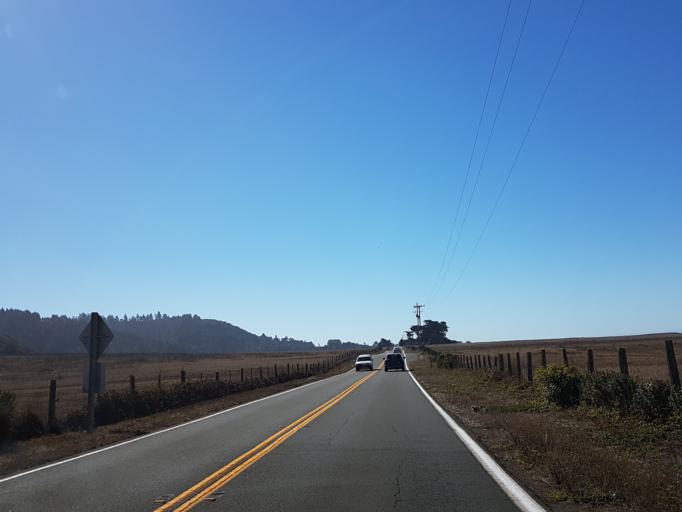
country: US
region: California
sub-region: Mendocino County
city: Boonville
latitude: 39.0487
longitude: -123.6849
